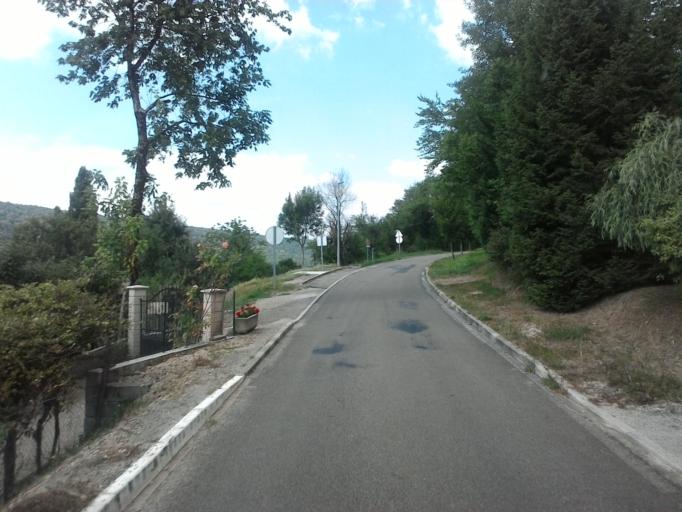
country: FR
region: Franche-Comte
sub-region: Departement du Doubs
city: Boussieres
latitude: 47.1214
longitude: 5.9231
